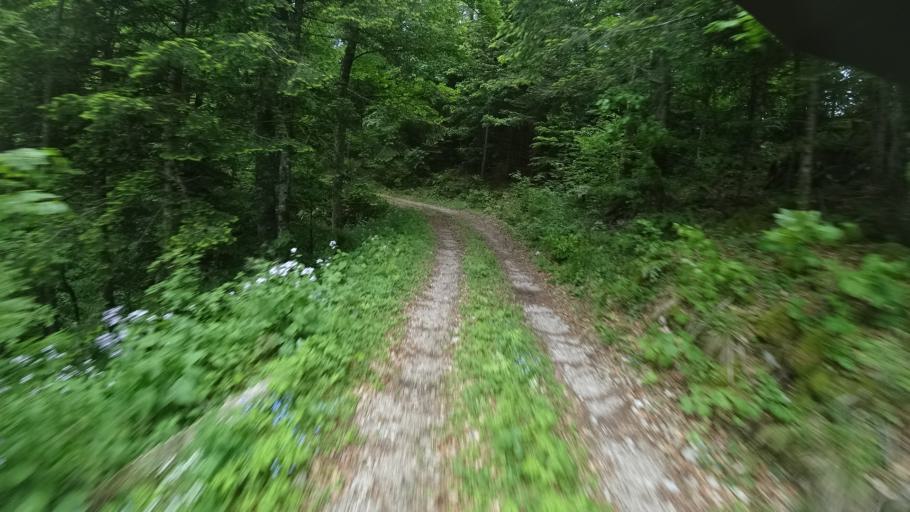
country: HR
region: Zadarska
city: Gracac
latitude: 44.4785
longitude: 15.8893
